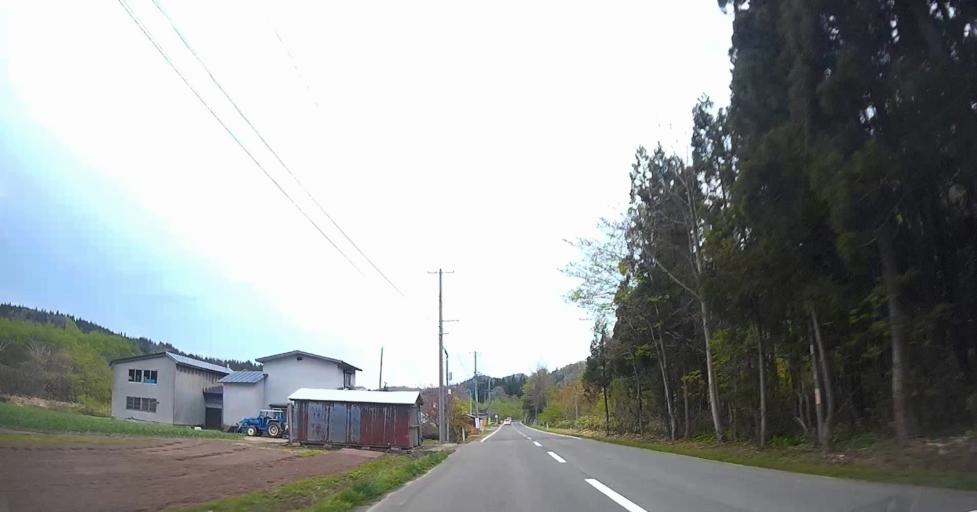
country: JP
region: Aomori
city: Goshogawara
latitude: 41.1304
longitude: 140.5197
